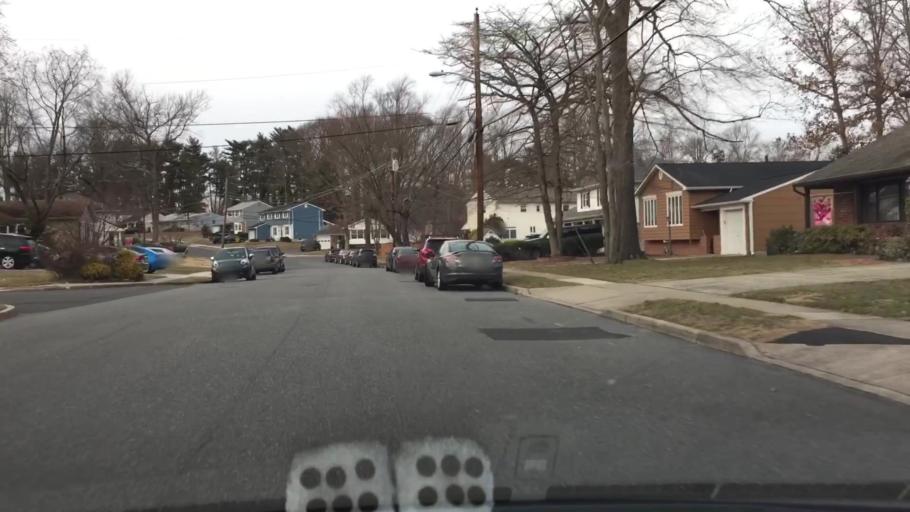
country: US
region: New Jersey
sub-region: Gloucester County
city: Turnersville
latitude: 39.7612
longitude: -75.0579
